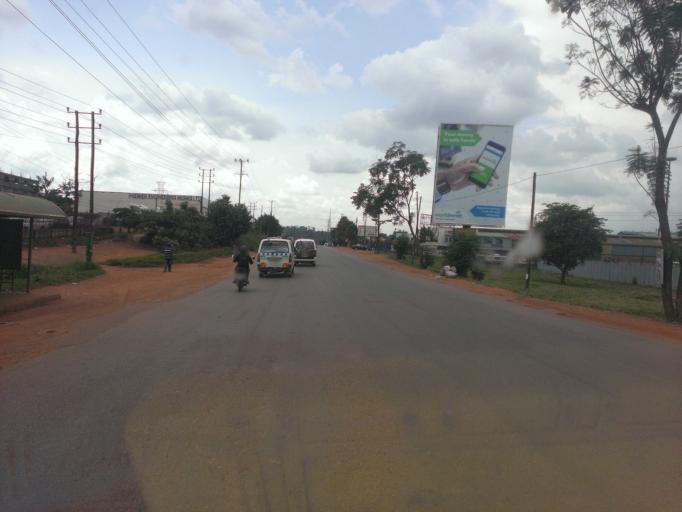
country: UG
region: Central Region
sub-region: Wakiso District
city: Kireka
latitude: 0.3344
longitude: 32.6187
